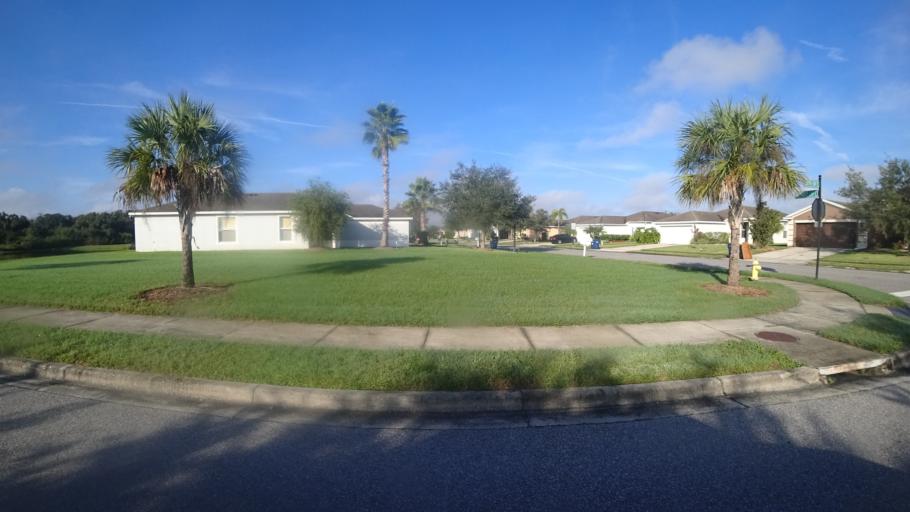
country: US
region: Florida
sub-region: Manatee County
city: Ellenton
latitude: 27.5589
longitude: -82.4599
